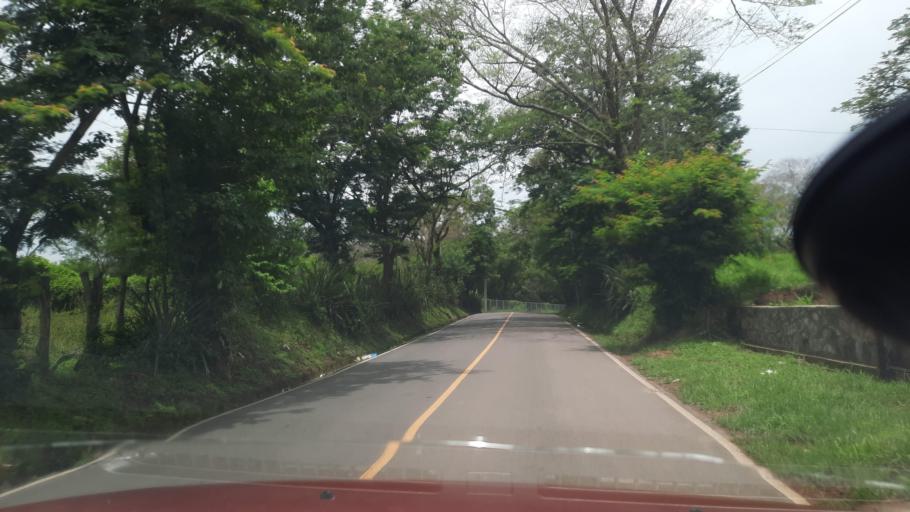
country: SV
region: La Union
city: Santa Rosa de Lima
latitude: 13.6468
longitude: -87.8546
